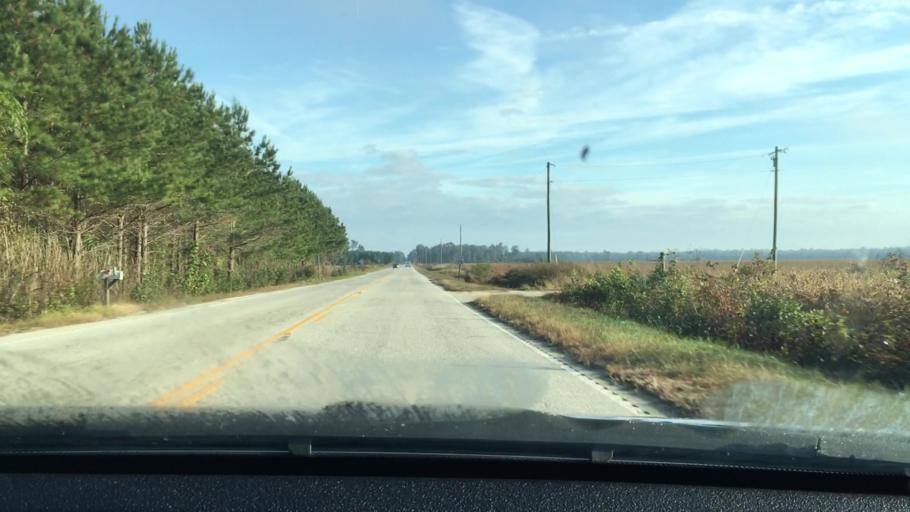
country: US
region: South Carolina
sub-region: Sumter County
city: East Sumter
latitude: 34.0094
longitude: -80.2861
